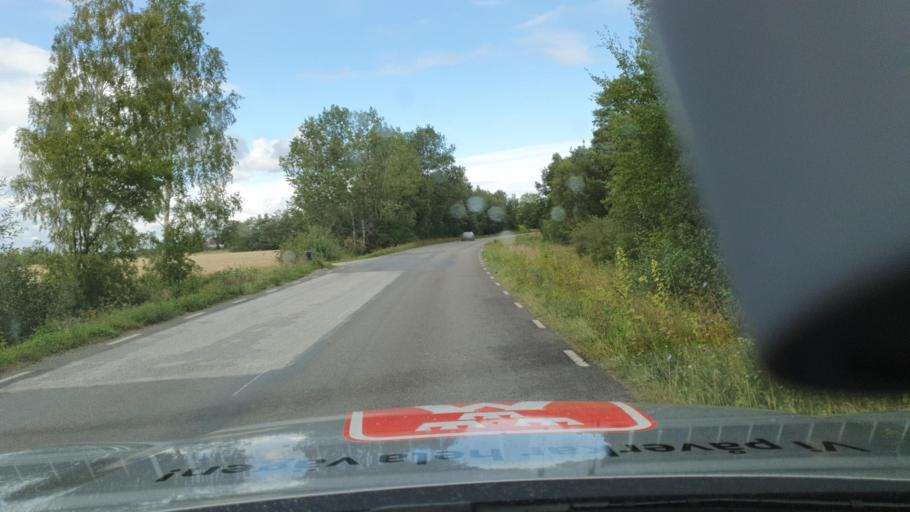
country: SE
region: Gotland
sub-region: Gotland
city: Hemse
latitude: 57.0158
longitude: 18.2569
